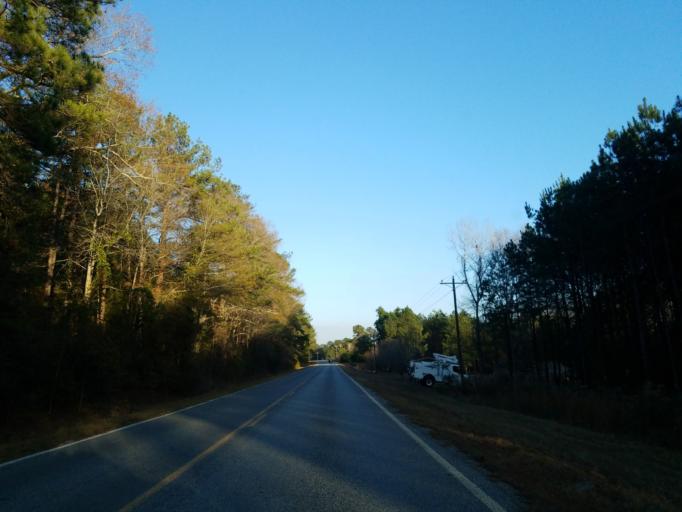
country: US
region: Mississippi
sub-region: Clarke County
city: Stonewall
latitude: 32.1673
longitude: -88.8512
